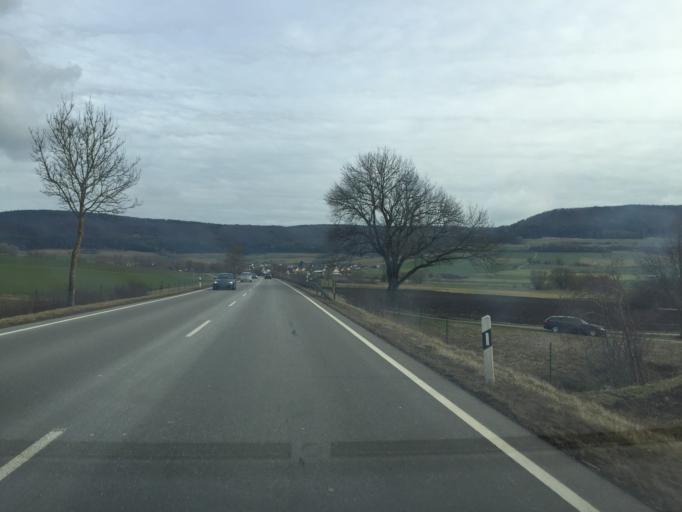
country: DE
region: Baden-Wuerttemberg
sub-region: Freiburg Region
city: Geisingen
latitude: 47.9224
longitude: 8.5978
